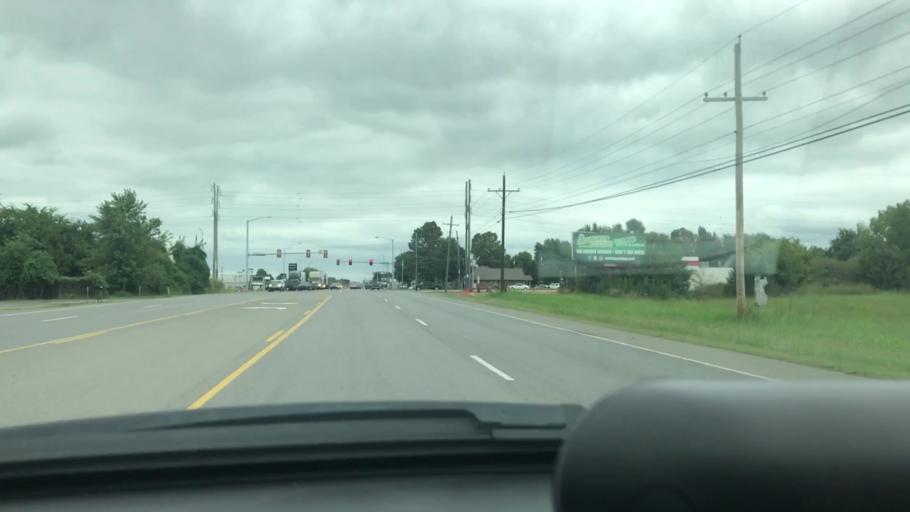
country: US
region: Oklahoma
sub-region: Wagoner County
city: Wagoner
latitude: 35.9429
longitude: -95.3952
